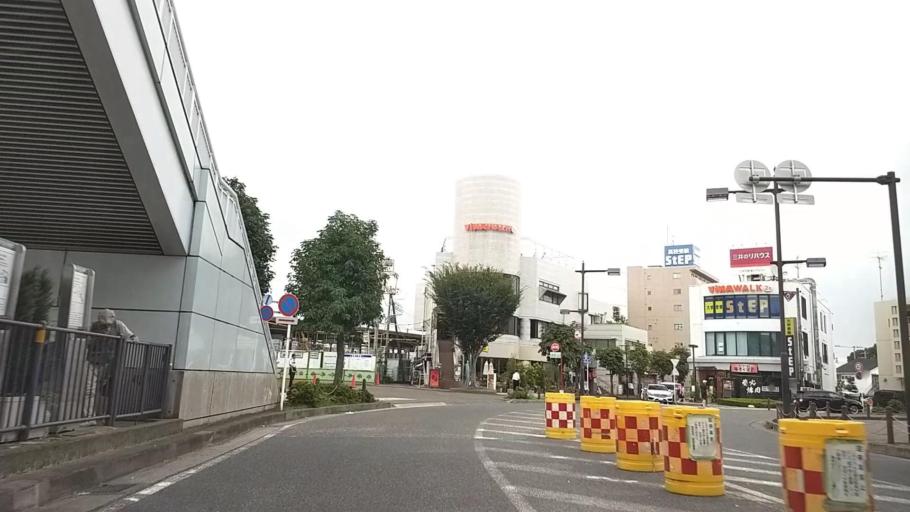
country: JP
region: Kanagawa
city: Atsugi
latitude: 35.4529
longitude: 139.3925
